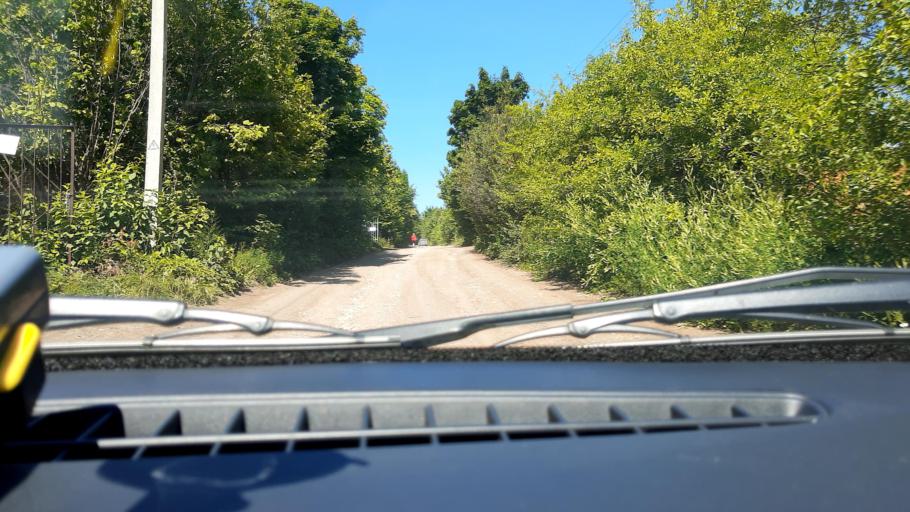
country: RU
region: Bashkortostan
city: Karmaskaly
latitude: 54.3628
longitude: 55.8924
